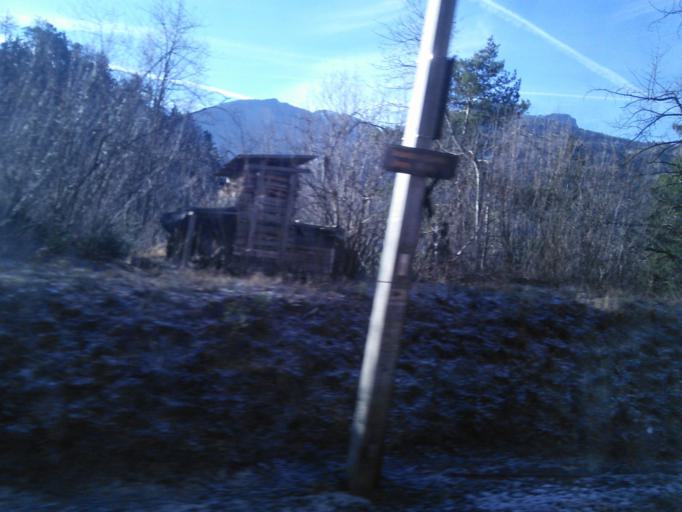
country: AT
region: Tyrol
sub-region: Politischer Bezirk Innsbruck Land
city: Mutters
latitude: 47.2127
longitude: 11.3959
